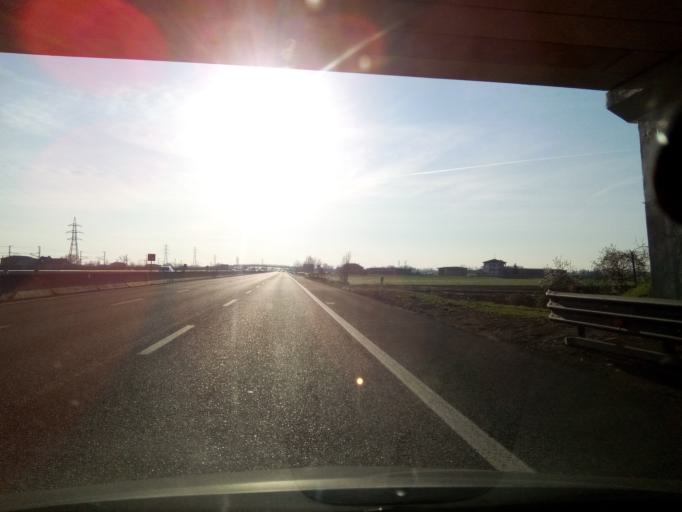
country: IT
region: Emilia-Romagna
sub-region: Provincia di Parma
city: Fidenza
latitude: 44.8943
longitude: 10.0561
